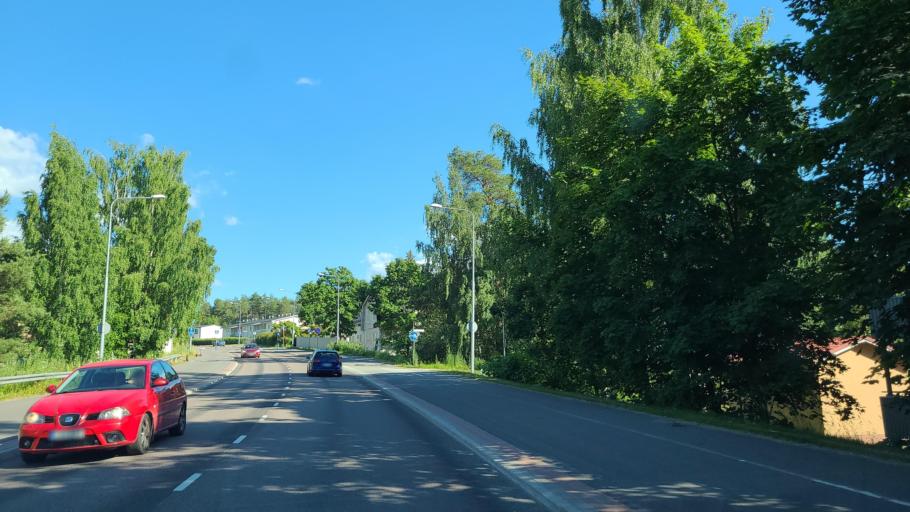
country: FI
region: Central Finland
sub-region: Jyvaeskylae
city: Jyvaeskylae
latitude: 62.2442
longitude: 25.7880
